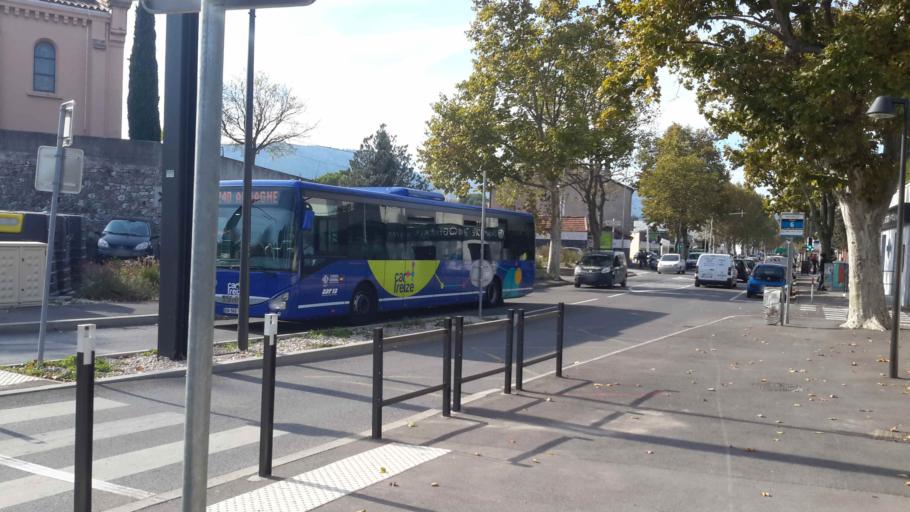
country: FR
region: Provence-Alpes-Cote d'Azur
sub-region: Departement des Bouches-du-Rhone
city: Aubagne
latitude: 43.2845
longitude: 5.5473
